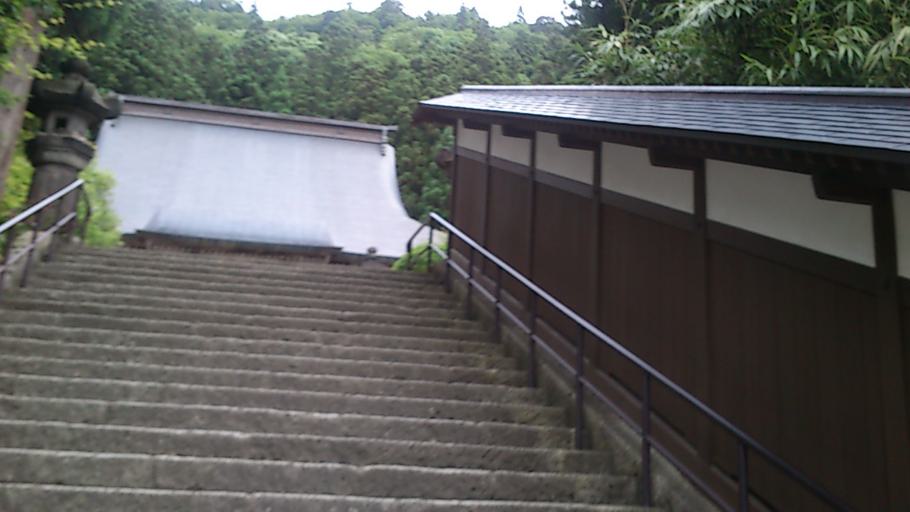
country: JP
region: Yamagata
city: Tendo
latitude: 38.3121
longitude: 140.4375
